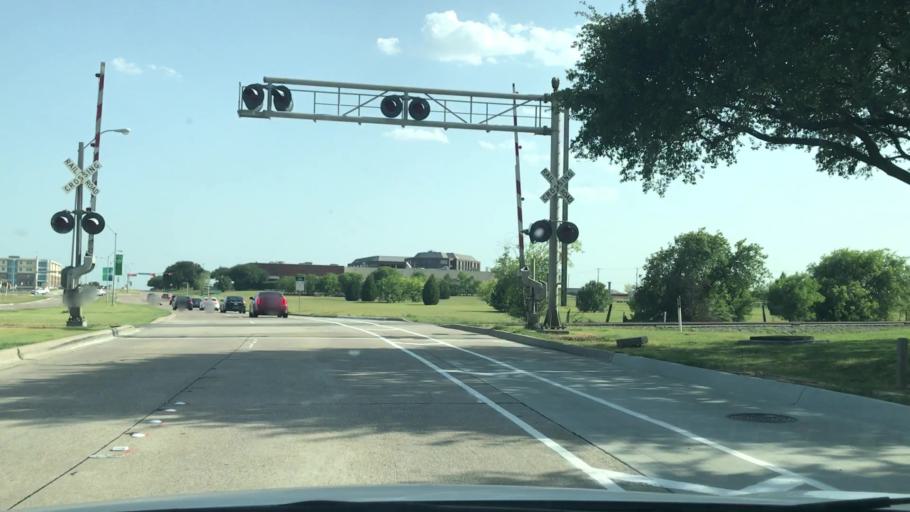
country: US
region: Texas
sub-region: Dallas County
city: Richardson
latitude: 32.9954
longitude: -96.7564
